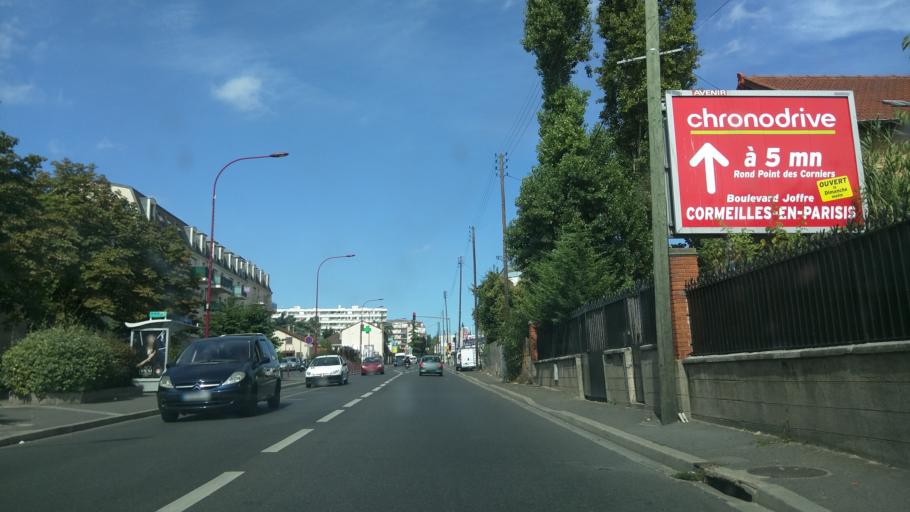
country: FR
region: Ile-de-France
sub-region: Departement du Val-d'Oise
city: Bezons
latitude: 48.9333
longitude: 2.2101
